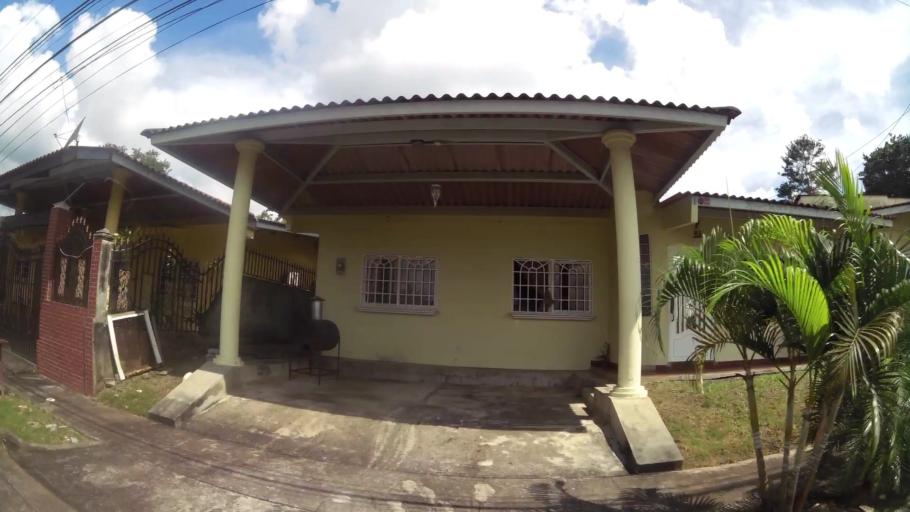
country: PA
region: Panama
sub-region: Distrito Arraijan
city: Arraijan
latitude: 8.9451
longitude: -79.6753
